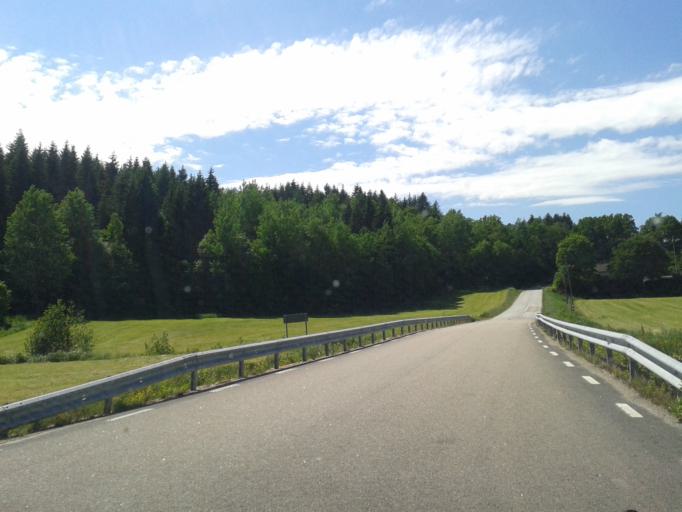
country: SE
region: Vaestra Goetaland
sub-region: Uddevalla Kommun
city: Uddevalla
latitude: 58.3024
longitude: 11.9663
